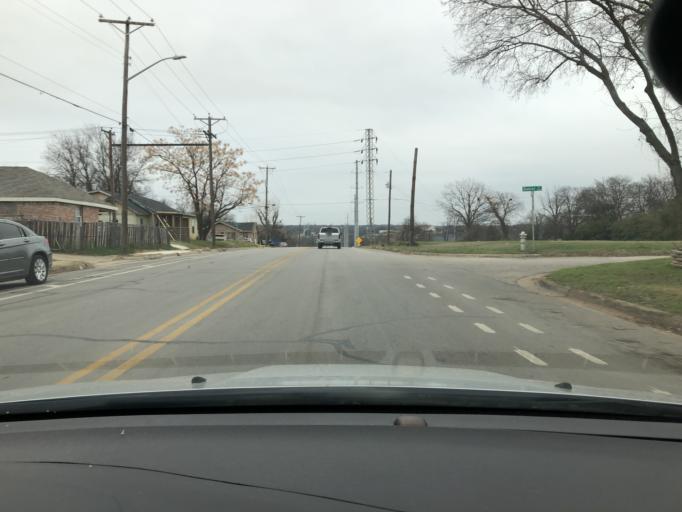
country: US
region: Texas
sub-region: Tarrant County
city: Fort Worth
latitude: 32.7268
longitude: -97.3016
